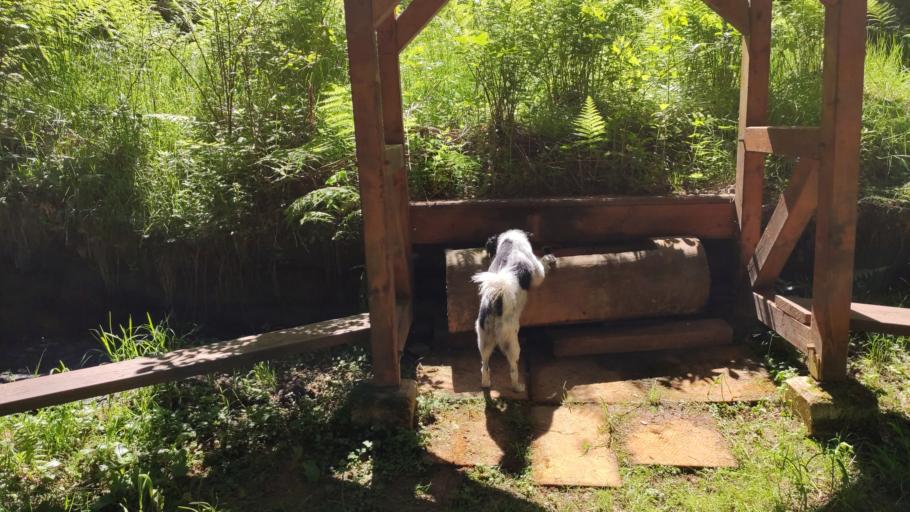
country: DE
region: Bavaria
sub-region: Upper Franconia
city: Tschirn
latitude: 50.4269
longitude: 11.4524
